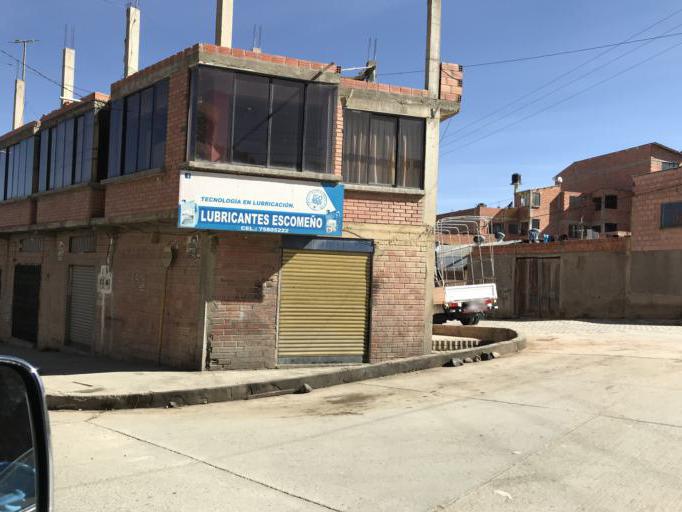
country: BO
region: La Paz
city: La Paz
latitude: -16.4867
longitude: -68.1806
